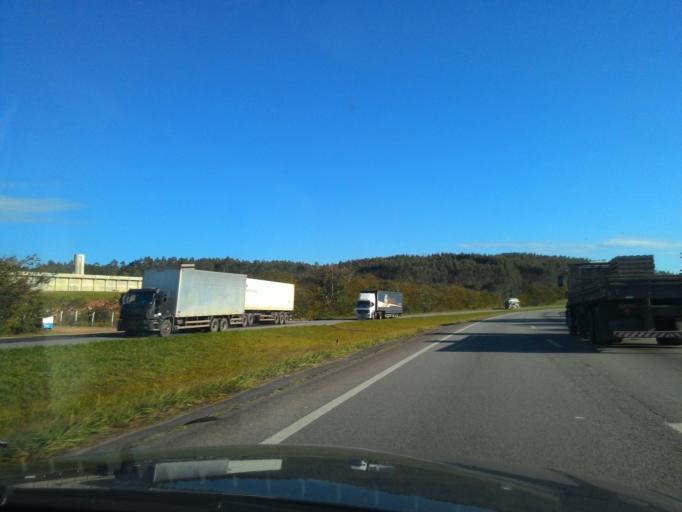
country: BR
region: Sao Paulo
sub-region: Registro
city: Registro
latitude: -24.5634
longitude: -47.8690
